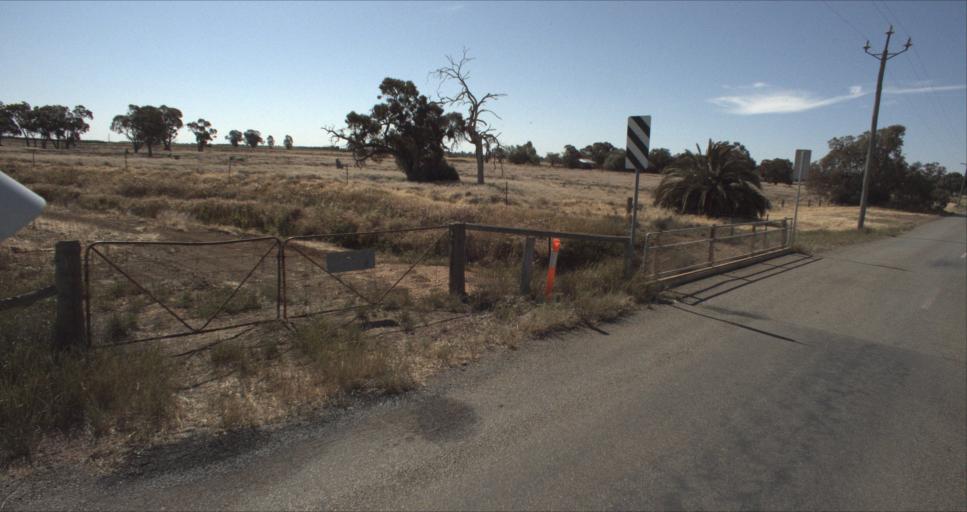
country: AU
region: New South Wales
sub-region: Leeton
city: Leeton
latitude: -34.5698
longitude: 146.3819
